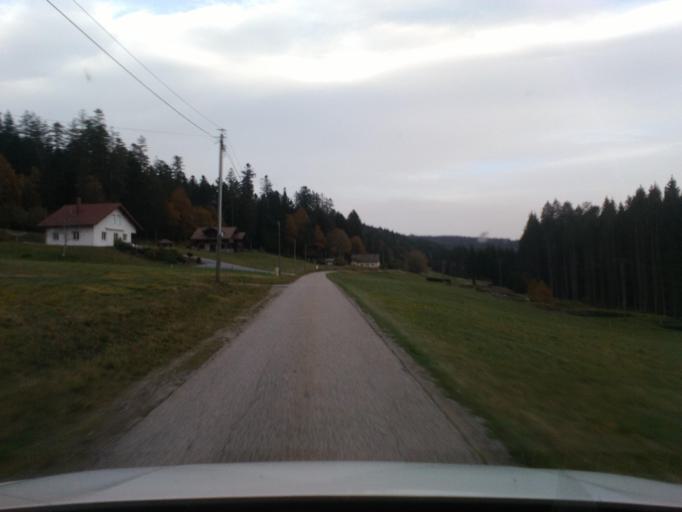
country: FR
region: Lorraine
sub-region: Departement des Vosges
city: Granges-sur-Vologne
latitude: 48.0956
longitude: 6.8183
